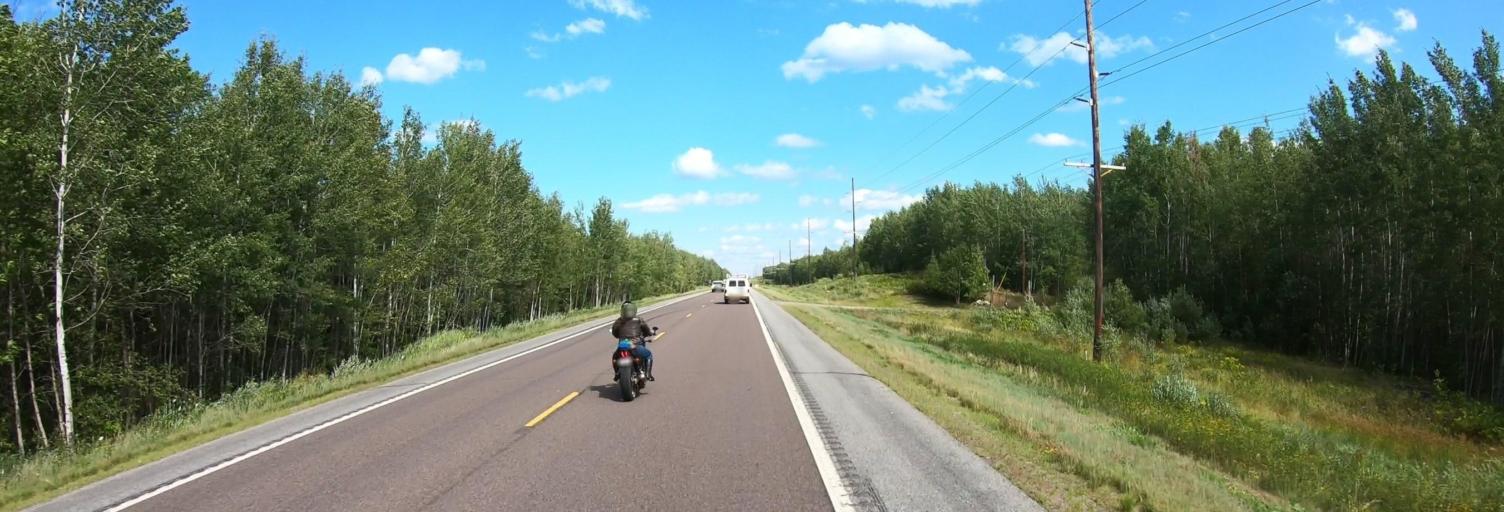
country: US
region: Minnesota
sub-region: Saint Louis County
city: Virginia
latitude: 47.8587
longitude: -92.4544
